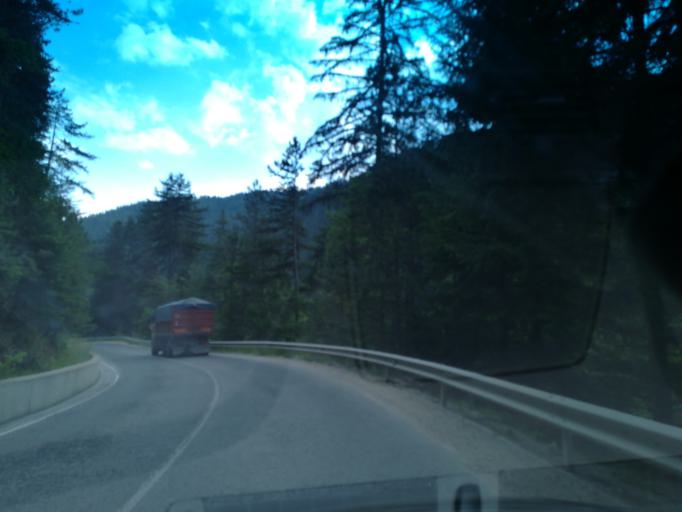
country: BG
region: Smolyan
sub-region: Obshtina Chepelare
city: Chepelare
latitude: 41.6681
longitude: 24.7494
